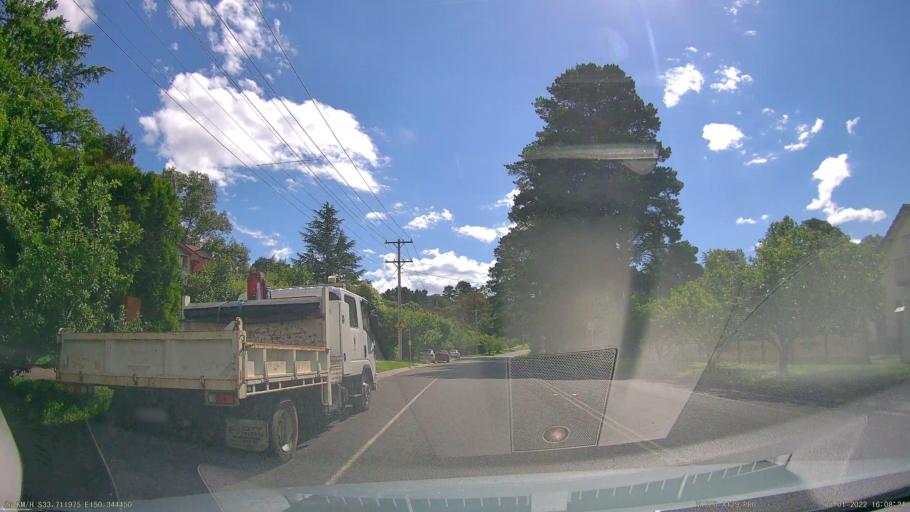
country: AU
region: New South Wales
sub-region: Blue Mountains Municipality
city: Leura
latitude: -33.7120
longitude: 150.3444
